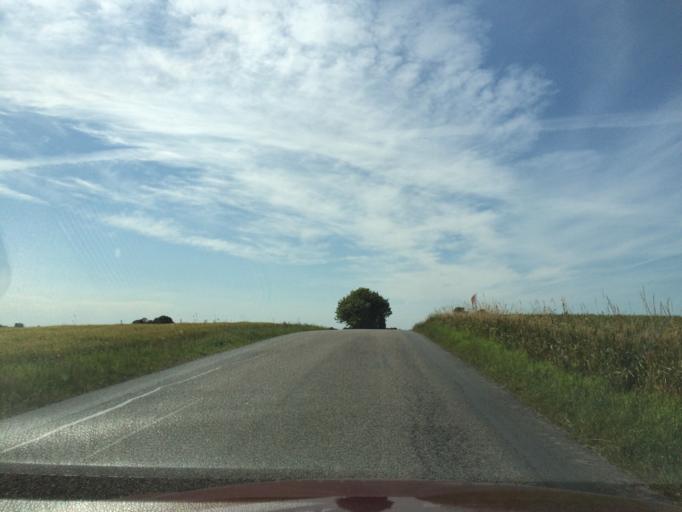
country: DK
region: Central Jutland
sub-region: Silkeborg Kommune
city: Silkeborg
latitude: 56.2261
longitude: 9.6085
